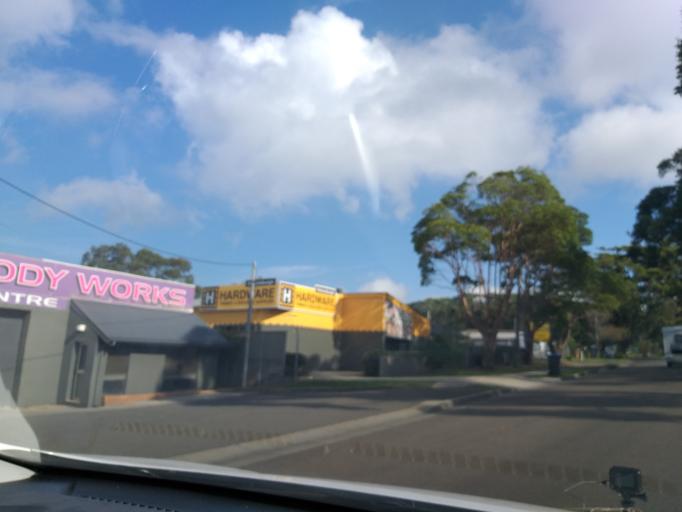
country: AU
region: New South Wales
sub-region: Wollongong
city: Helensburgh
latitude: -34.1955
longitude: 150.9753
